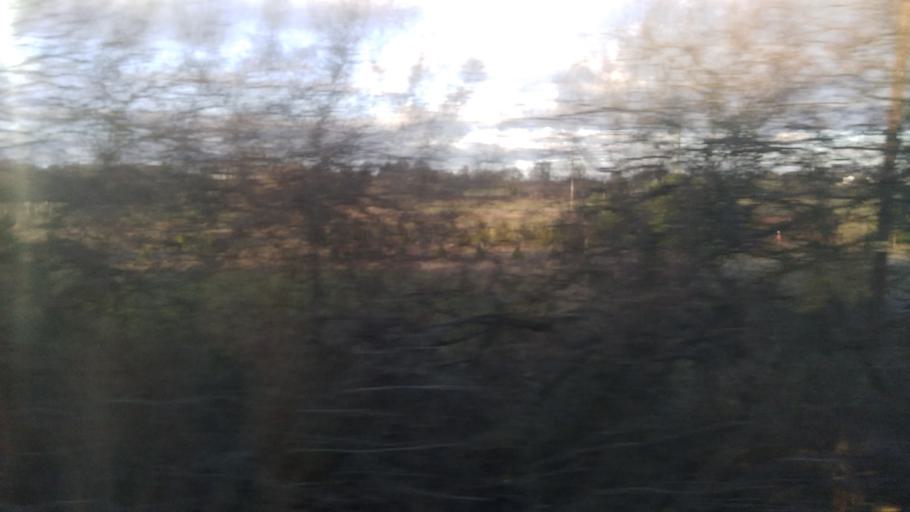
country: GB
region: England
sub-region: Kent
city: Headcorn
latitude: 51.1669
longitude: 0.6123
